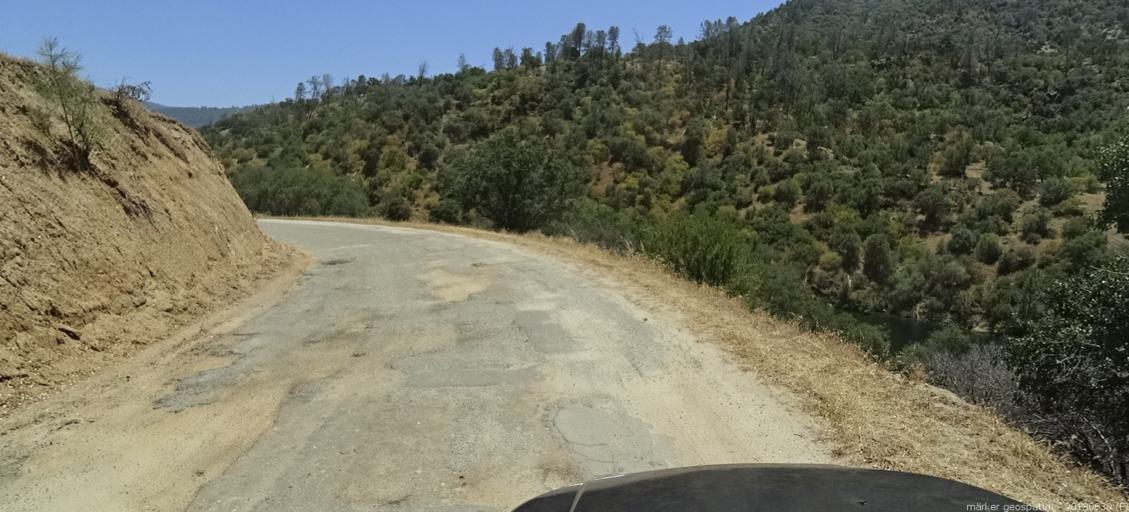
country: US
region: California
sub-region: Fresno County
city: Auberry
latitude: 37.1635
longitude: -119.4125
